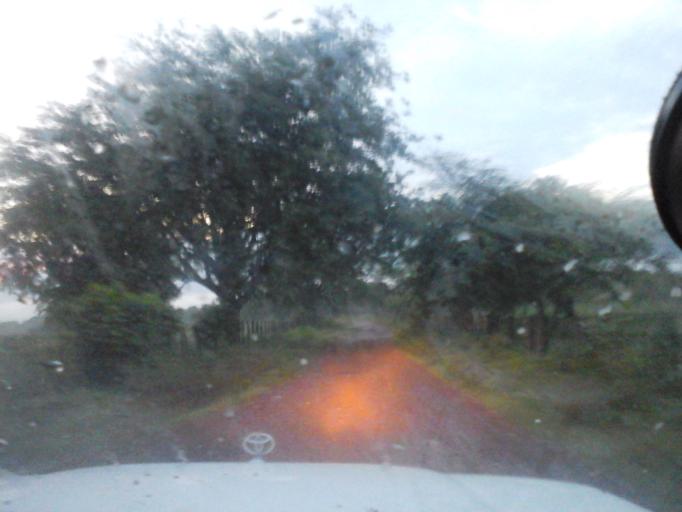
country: CO
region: Cesar
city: Agustin Codazzi
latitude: 10.1555
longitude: -73.2147
